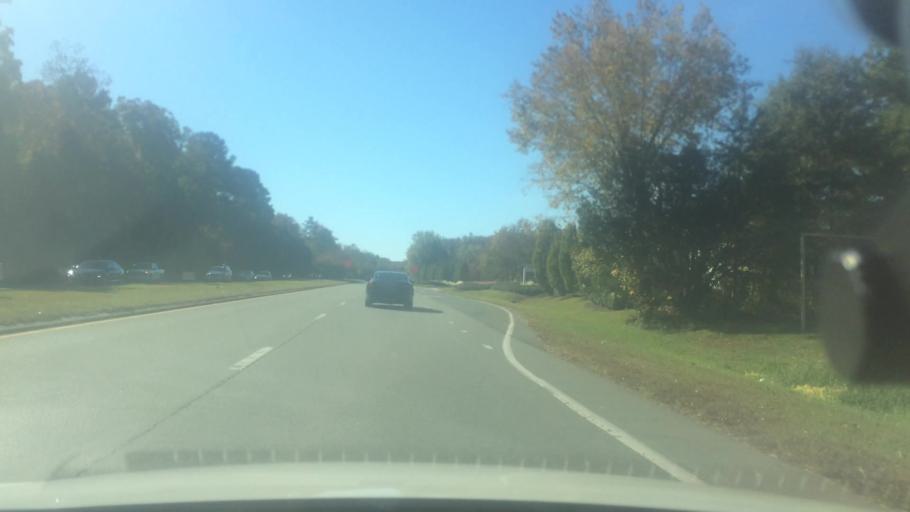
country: US
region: North Carolina
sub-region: Orange County
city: Chapel Hill
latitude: 35.9289
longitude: -79.0245
